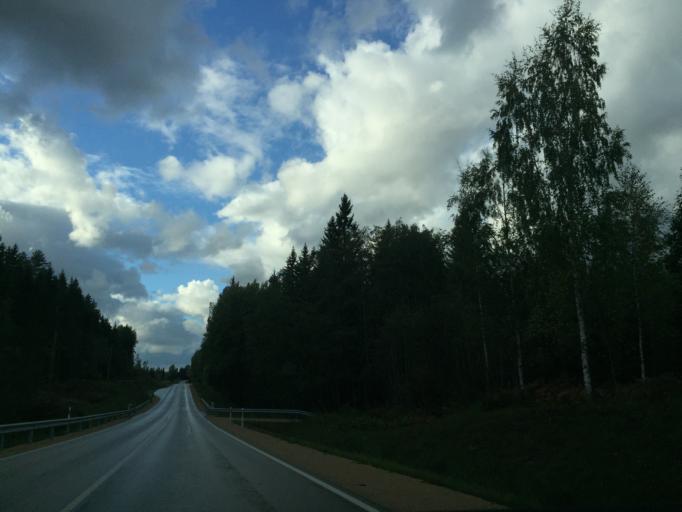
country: LV
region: Ligatne
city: Ligatne
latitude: 57.1586
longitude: 25.0612
